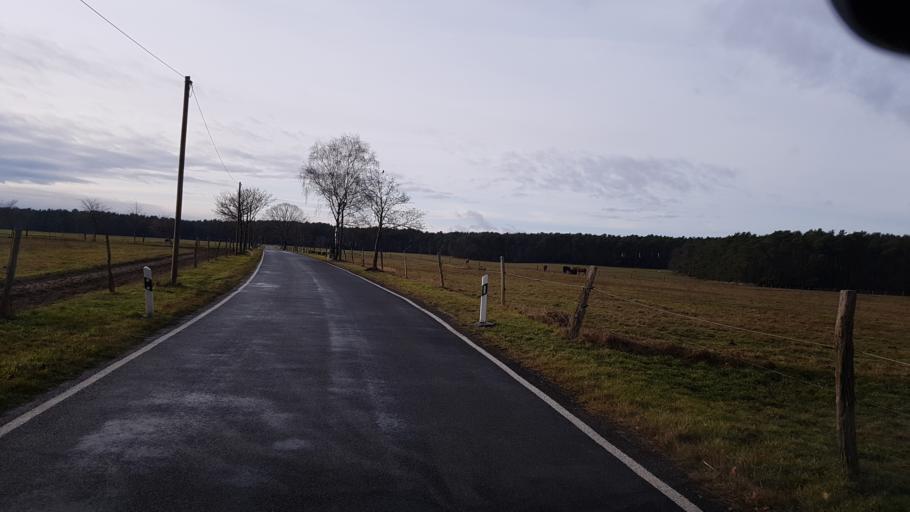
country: DE
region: Brandenburg
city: Altdobern
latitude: 51.6709
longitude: 13.9811
